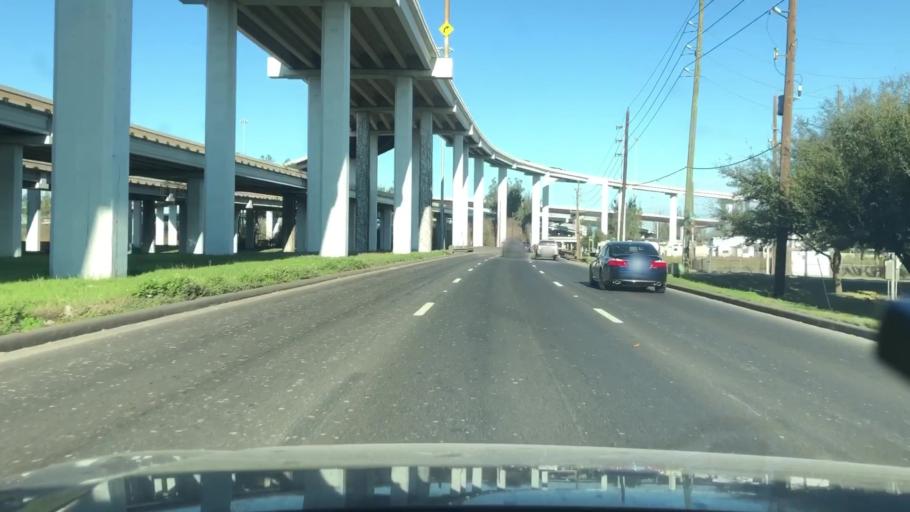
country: US
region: Texas
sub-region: Fort Bend County
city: Meadows Place
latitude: 29.6580
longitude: -95.5547
